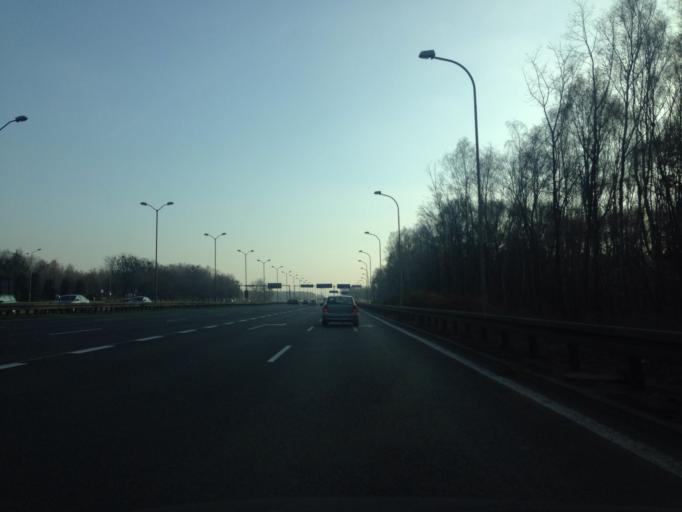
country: PL
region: Silesian Voivodeship
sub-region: Katowice
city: Katowice
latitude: 50.2480
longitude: 19.0496
